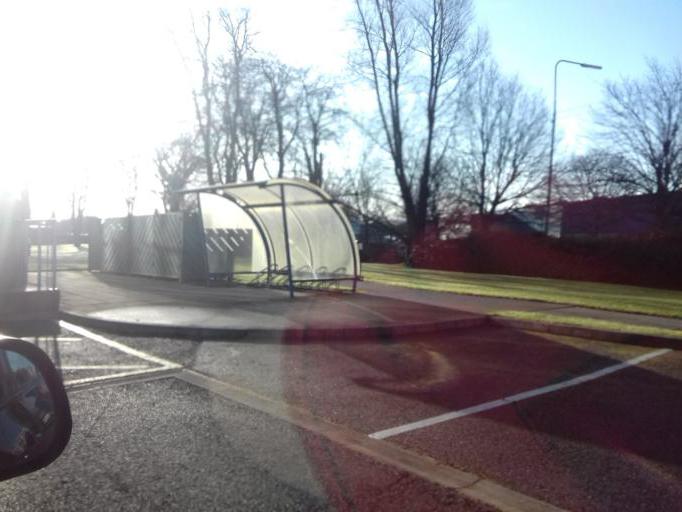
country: IE
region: Leinster
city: Beaumont
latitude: 53.4078
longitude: -6.2368
